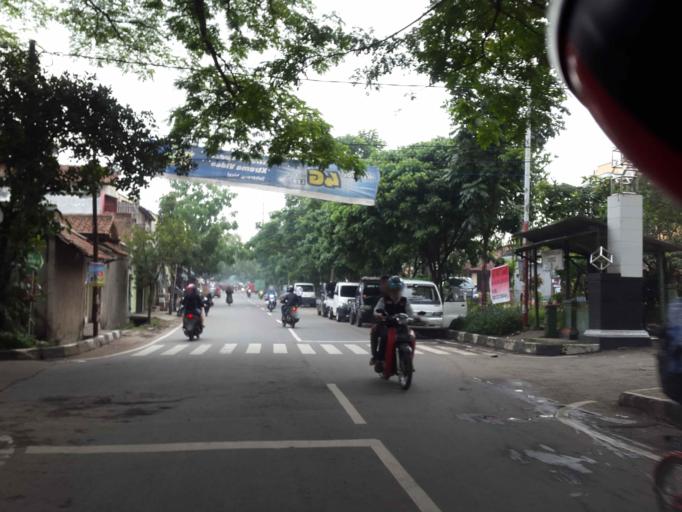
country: ID
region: West Java
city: Margahayukencana
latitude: -6.9238
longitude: 107.5629
